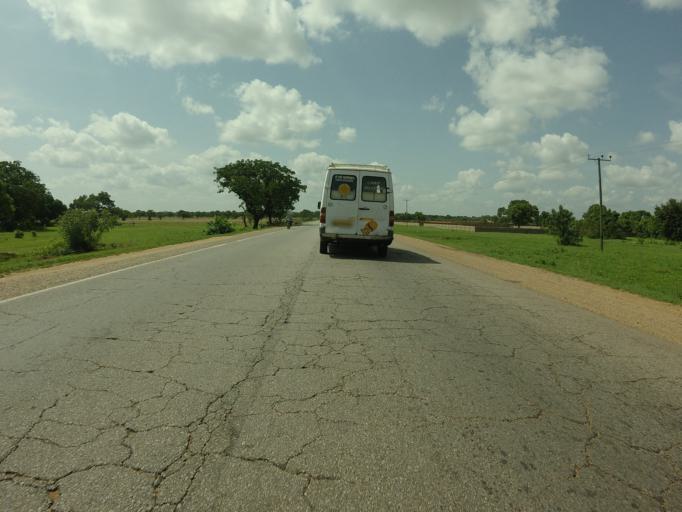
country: GH
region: Northern
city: Savelugu
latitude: 9.5651
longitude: -0.8358
